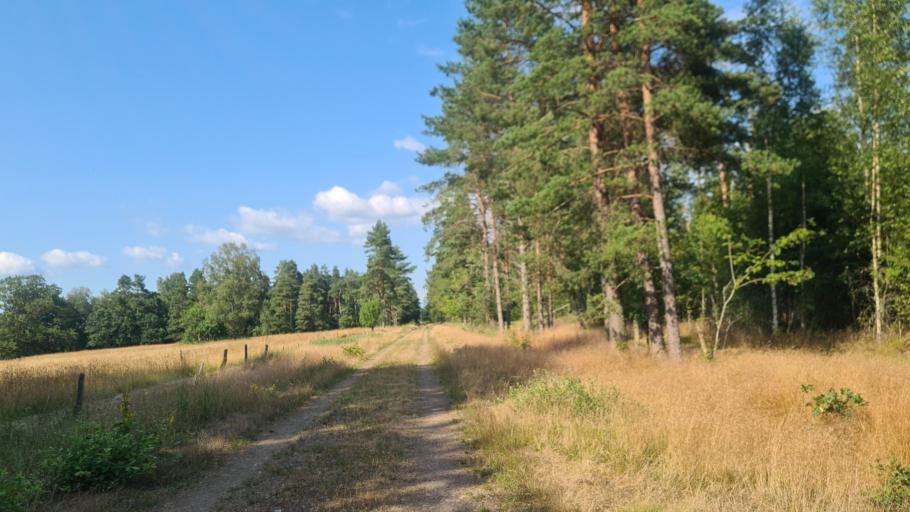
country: SE
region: Kronoberg
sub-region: Ljungby Kommun
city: Ljungby
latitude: 56.7661
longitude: 13.8941
